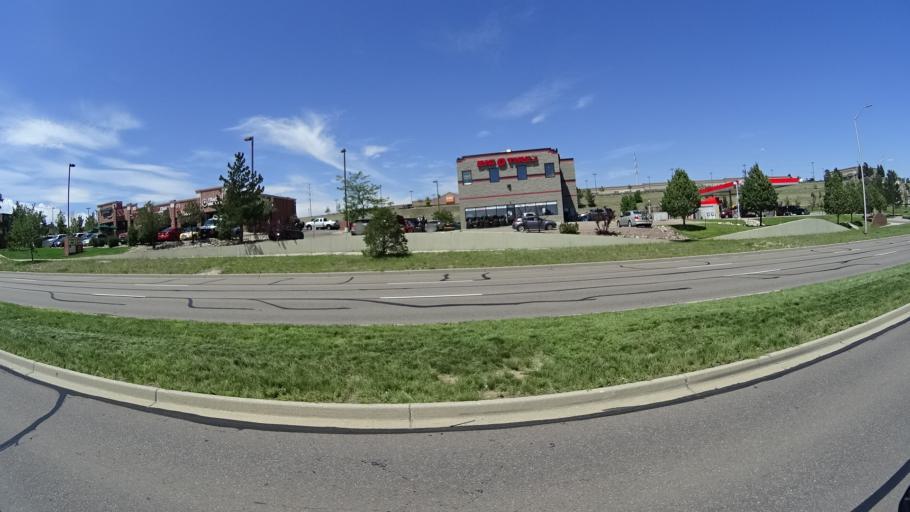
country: US
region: Colorado
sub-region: El Paso County
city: Black Forest
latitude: 38.9376
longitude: -104.7600
